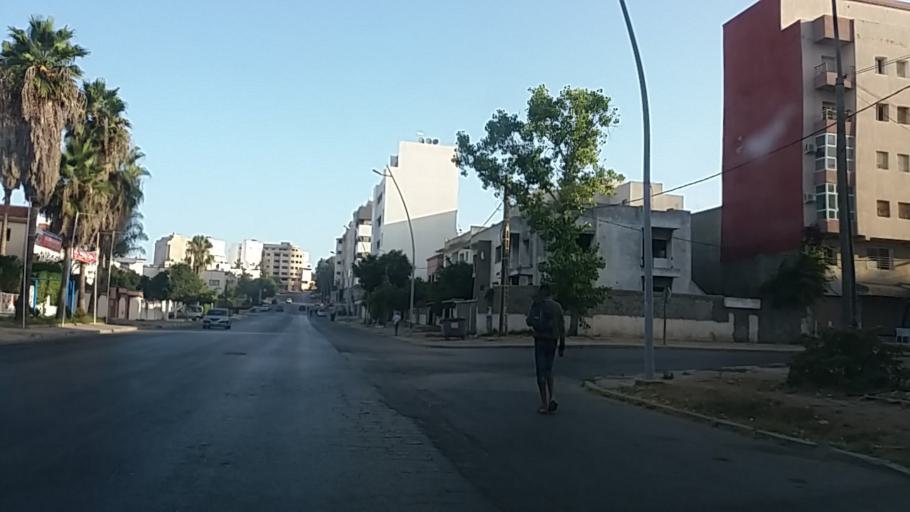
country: MA
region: Gharb-Chrarda-Beni Hssen
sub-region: Kenitra Province
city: Kenitra
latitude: 34.2573
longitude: -6.5977
